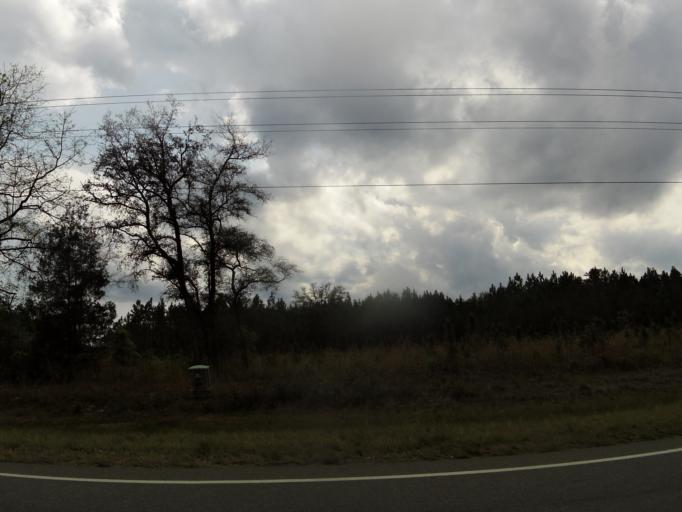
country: US
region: Georgia
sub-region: Charlton County
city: Folkston
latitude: 30.8271
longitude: -81.8689
